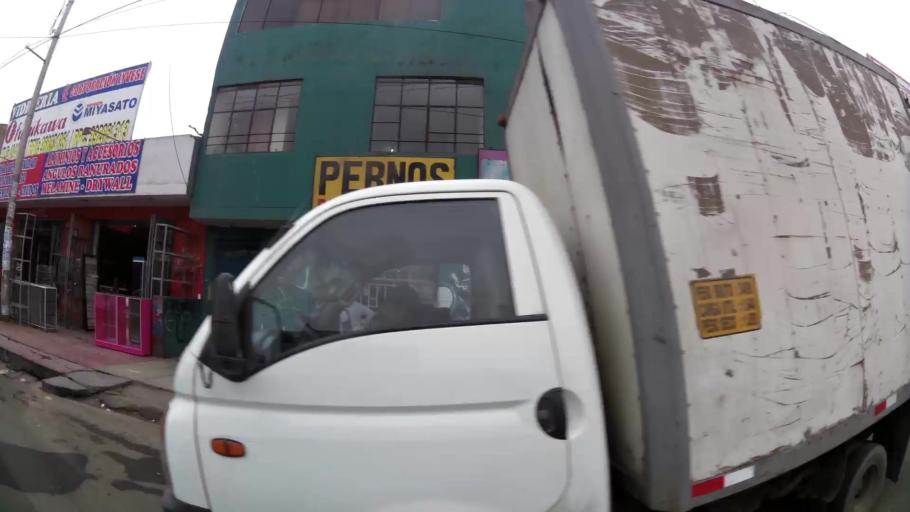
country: PE
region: Lima
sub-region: Lima
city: Vitarte
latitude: -12.0349
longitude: -76.9293
